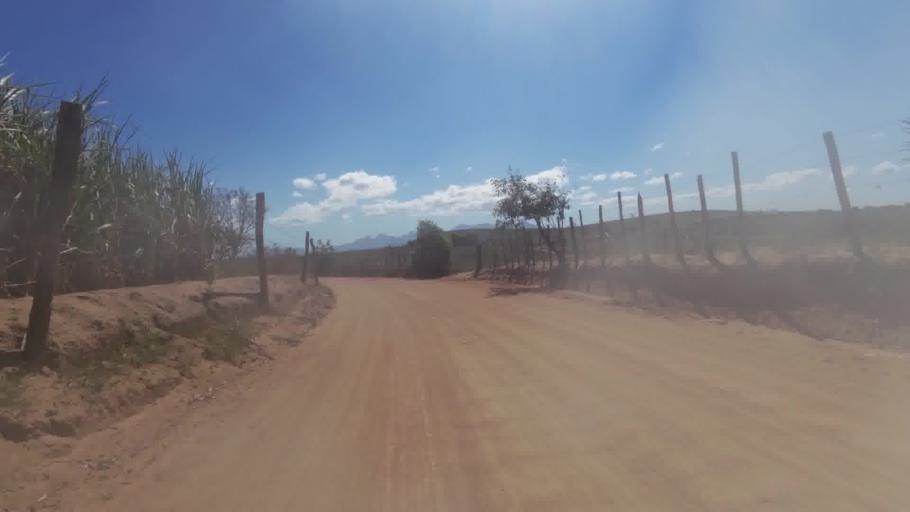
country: BR
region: Espirito Santo
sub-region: Marataizes
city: Marataizes
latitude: -21.1409
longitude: -40.9861
